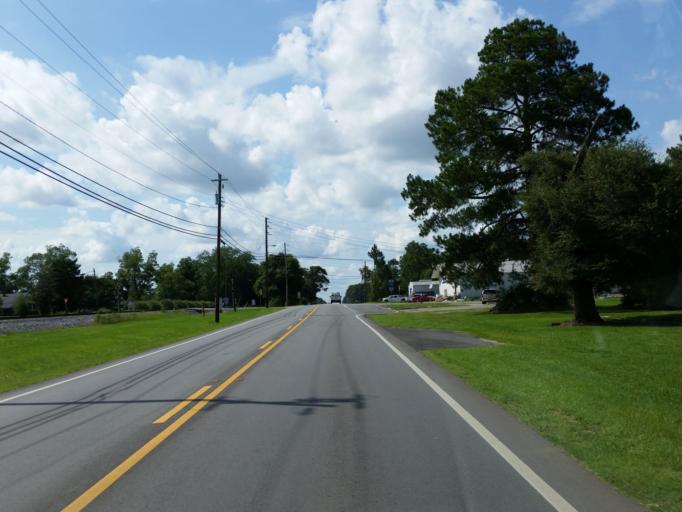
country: US
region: Georgia
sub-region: Turner County
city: Ashburn
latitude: 31.6747
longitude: -83.6377
